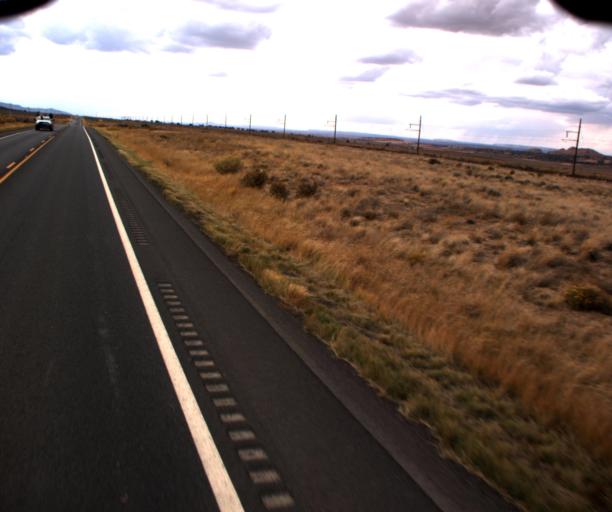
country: US
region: Arizona
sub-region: Navajo County
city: Kayenta
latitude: 36.5253
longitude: -110.5780
